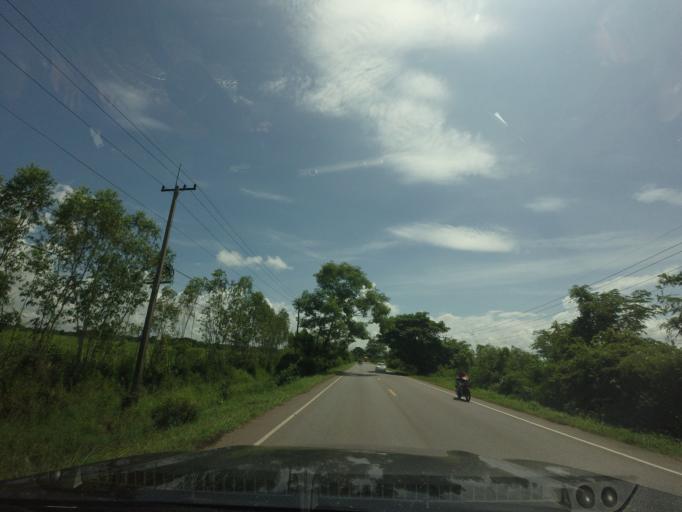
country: TH
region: Changwat Udon Thani
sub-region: Amphoe Ban Phue
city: Ban Phue
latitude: 17.7162
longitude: 102.4075
